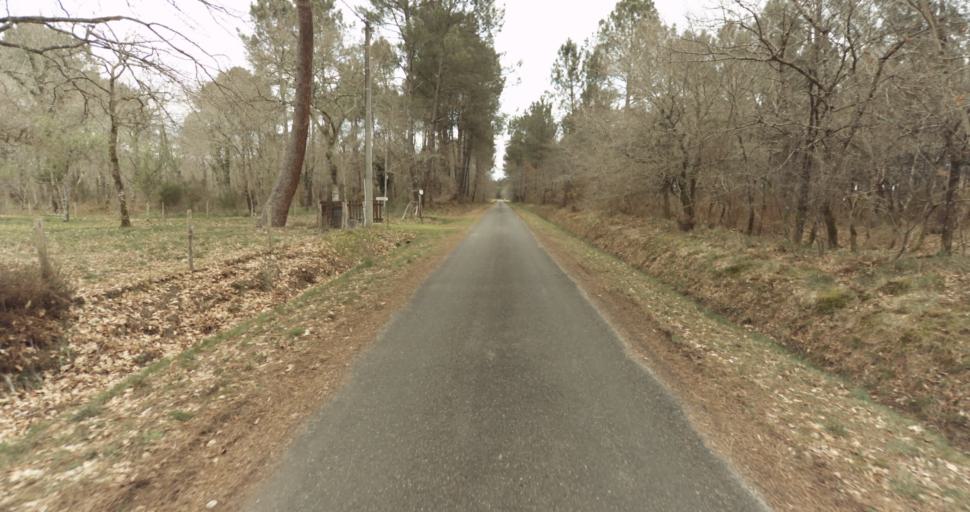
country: FR
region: Aquitaine
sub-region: Departement des Landes
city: Roquefort
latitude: 44.0766
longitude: -0.3800
